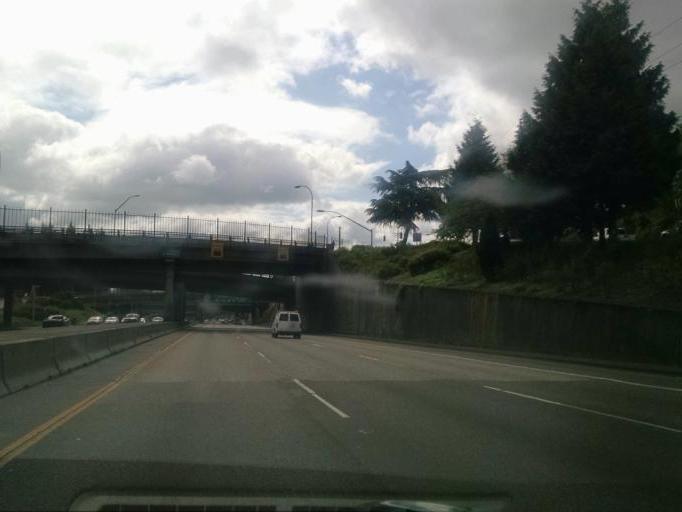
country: US
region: Oregon
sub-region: Multnomah County
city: Portland
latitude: 45.5091
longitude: -122.6865
